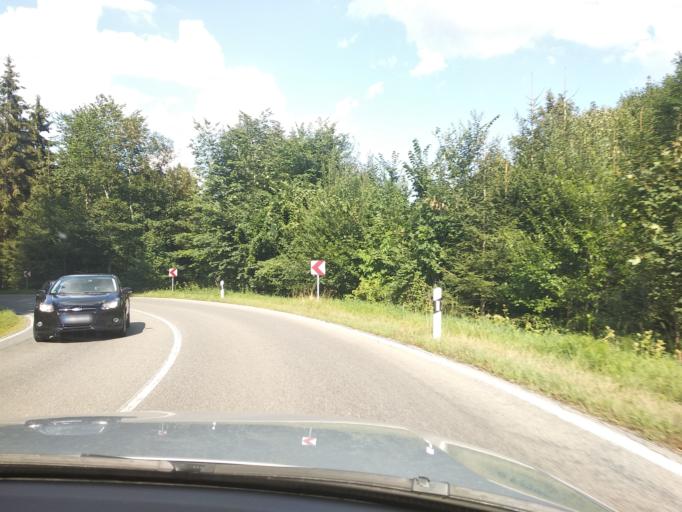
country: DE
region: Baden-Wuerttemberg
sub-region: Tuebingen Region
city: Leutkirch im Allgau
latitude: 47.8689
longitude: 10.0041
